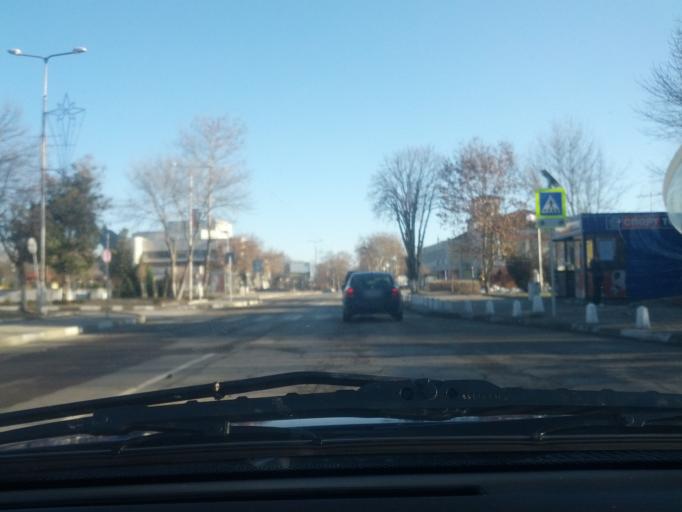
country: BG
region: Vratsa
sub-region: Obshtina Kozloduy
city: Kozloduy
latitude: 43.7775
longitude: 23.7295
